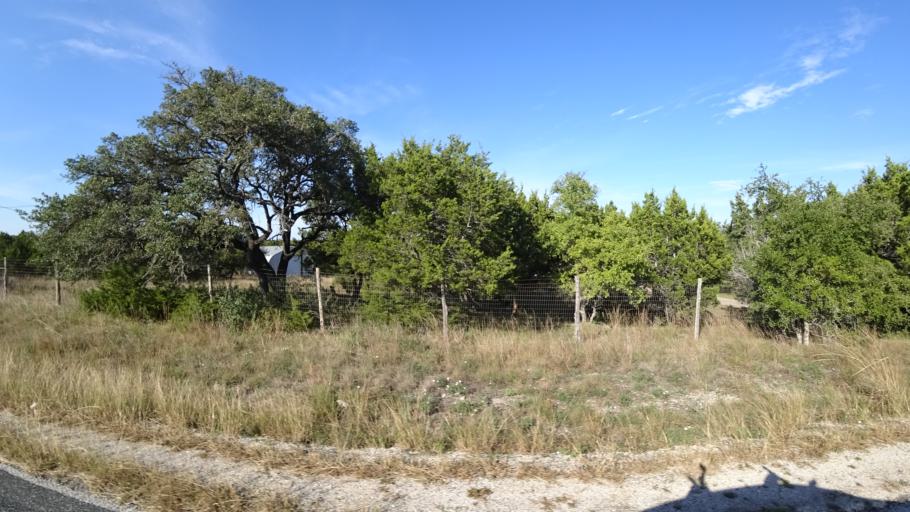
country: US
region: Texas
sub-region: Travis County
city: Bee Cave
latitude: 30.2349
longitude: -97.9288
